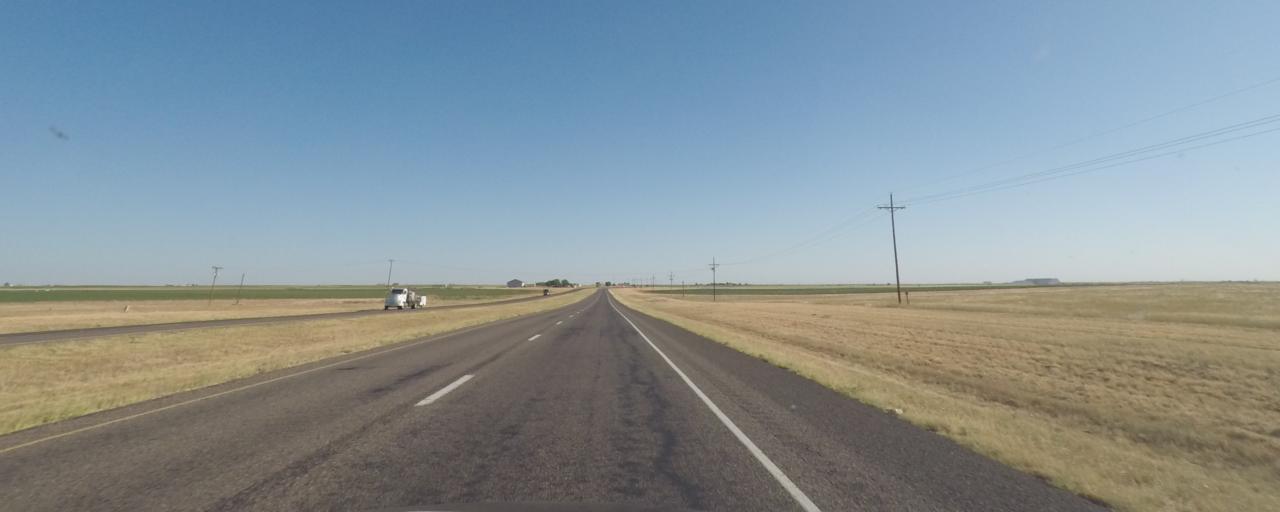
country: US
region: Texas
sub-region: Gaines County
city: Seagraves
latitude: 32.8626
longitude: -102.6404
